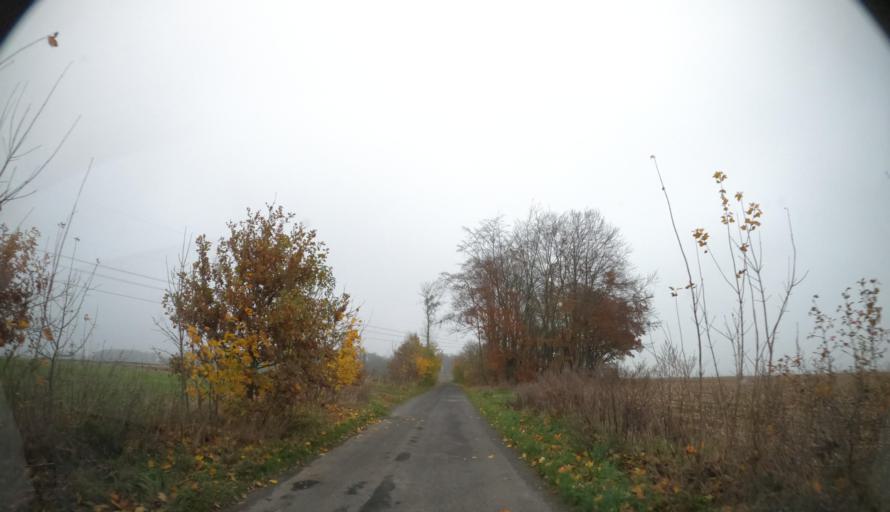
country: PL
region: West Pomeranian Voivodeship
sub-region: Powiat lobeski
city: Radowo Male
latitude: 53.6705
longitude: 15.4476
